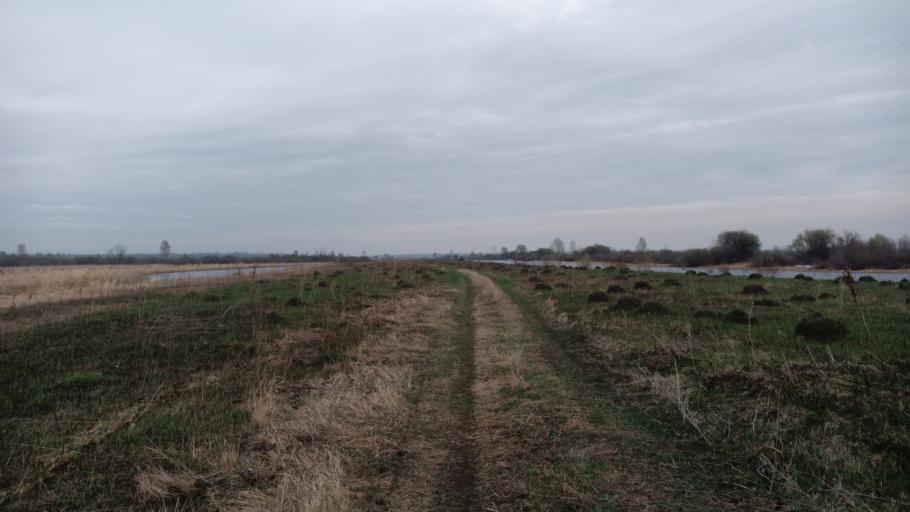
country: RU
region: Altai Krai
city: Yuzhnyy
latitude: 53.2235
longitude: 83.7382
